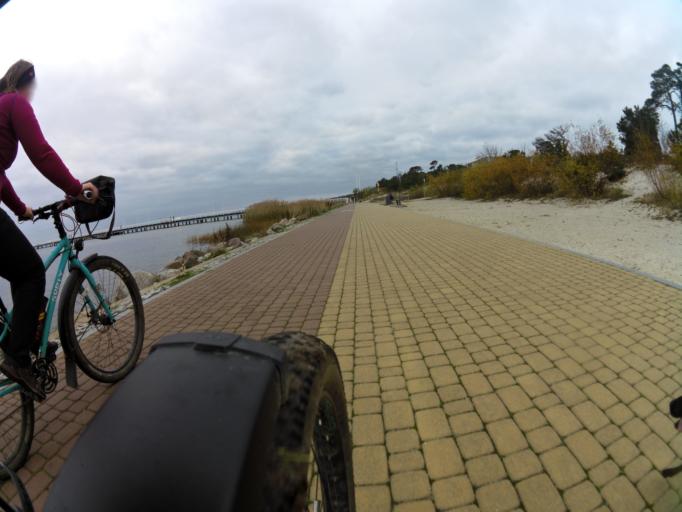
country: PL
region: Pomeranian Voivodeship
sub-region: Powiat pucki
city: Jastarnia
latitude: 54.6810
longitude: 18.7120
